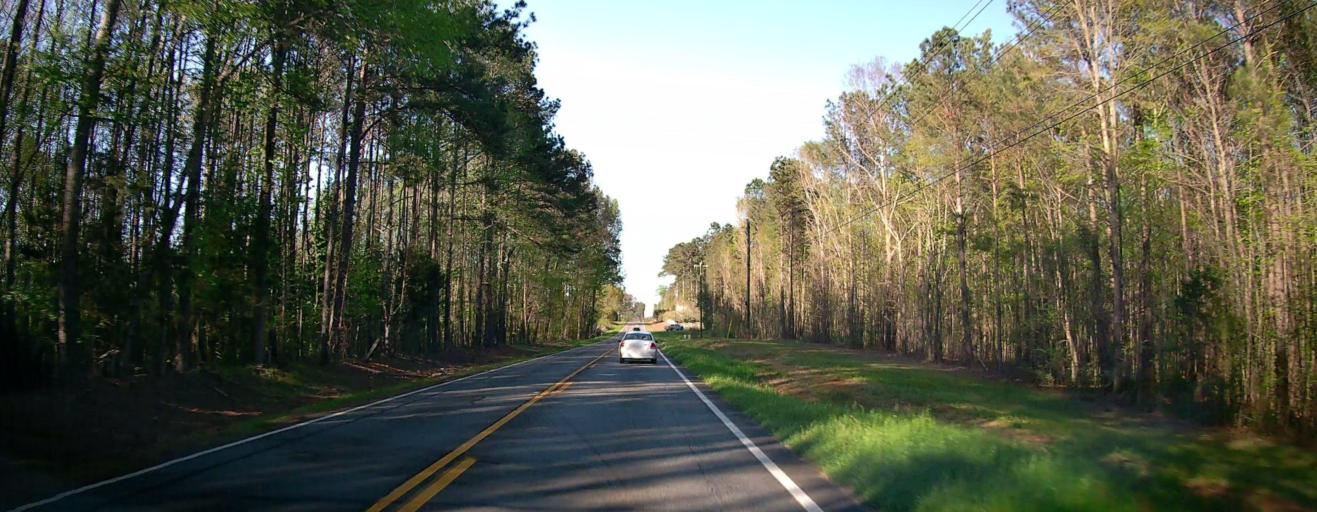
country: US
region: Georgia
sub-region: Monroe County
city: Forsyth
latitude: 33.0888
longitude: -83.9495
